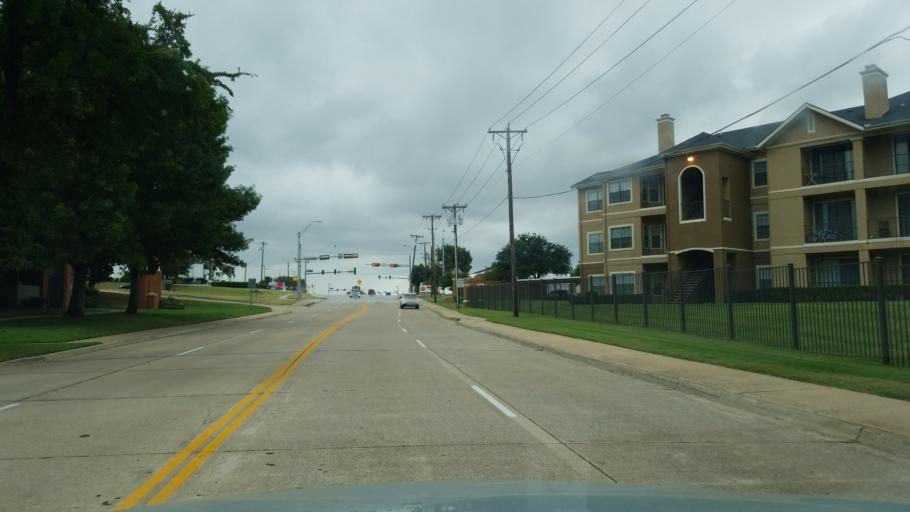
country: US
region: Texas
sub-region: Tarrant County
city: Bedford
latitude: 32.8419
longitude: -97.1223
